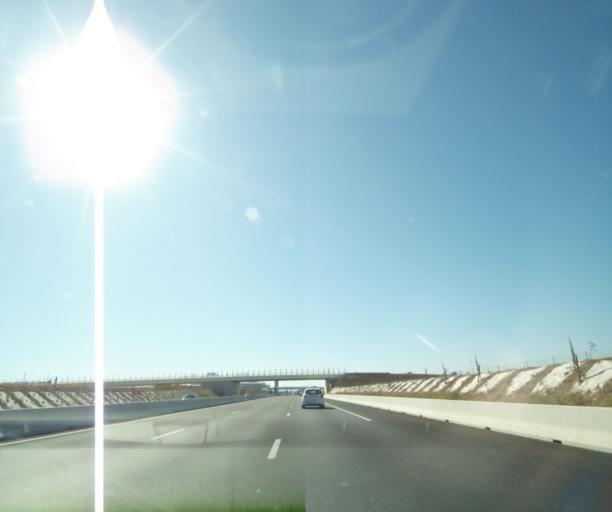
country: FR
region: Languedoc-Roussillon
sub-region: Departement de l'Herault
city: Lattes
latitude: 43.5985
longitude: 3.9297
